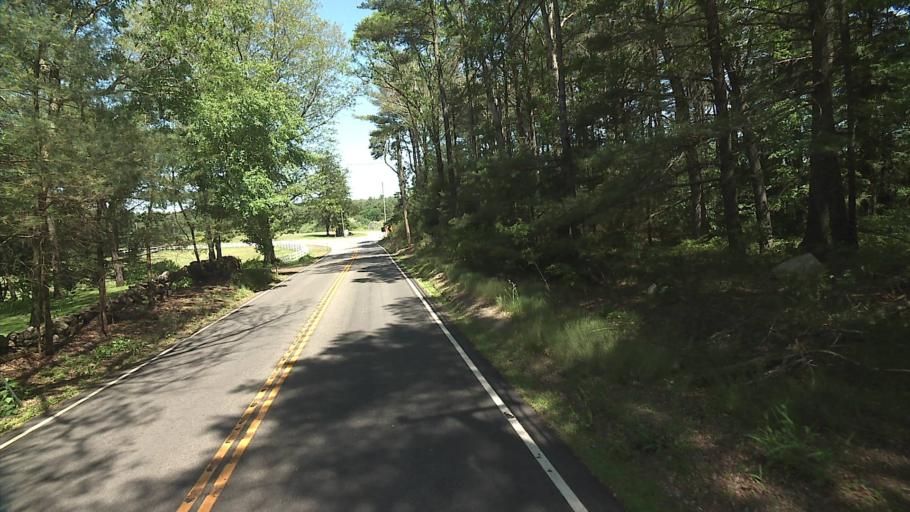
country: US
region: Rhode Island
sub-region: Washington County
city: Hopkinton
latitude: 41.5496
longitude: -71.8457
